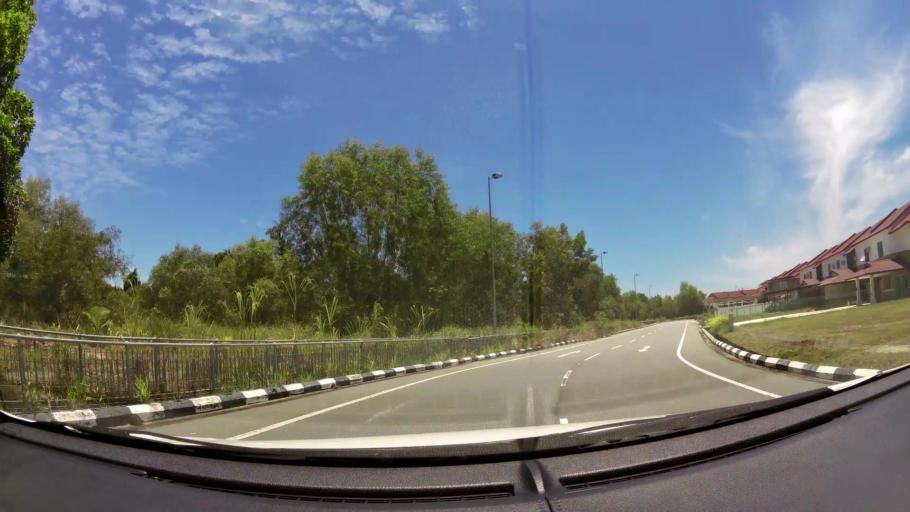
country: BN
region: Brunei and Muara
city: Bandar Seri Begawan
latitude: 5.0116
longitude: 115.0070
